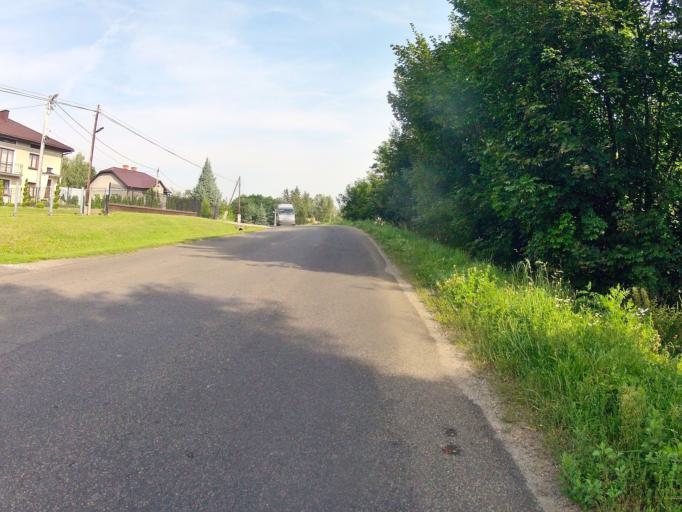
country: PL
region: Subcarpathian Voivodeship
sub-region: Powiat jasielski
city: Kolaczyce
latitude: 49.7850
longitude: 21.4036
